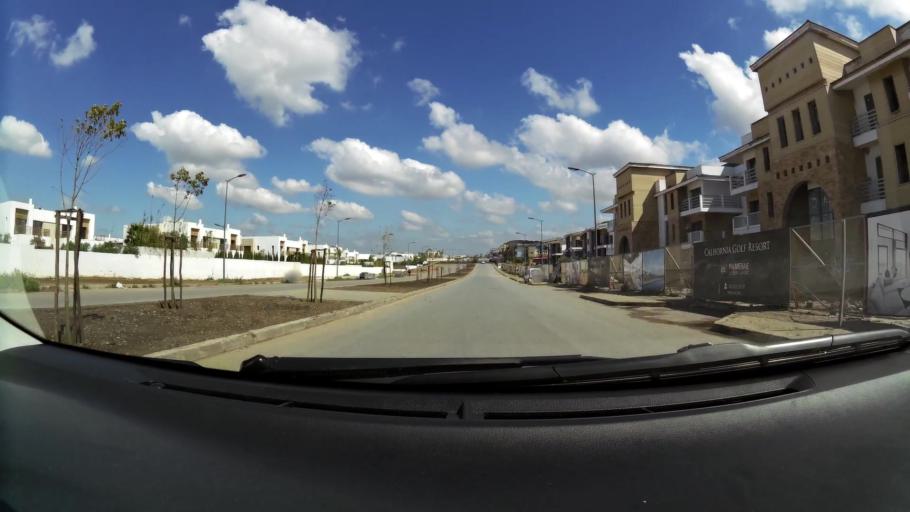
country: MA
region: Grand Casablanca
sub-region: Nouaceur
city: Bouskoura
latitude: 33.4876
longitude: -7.6034
